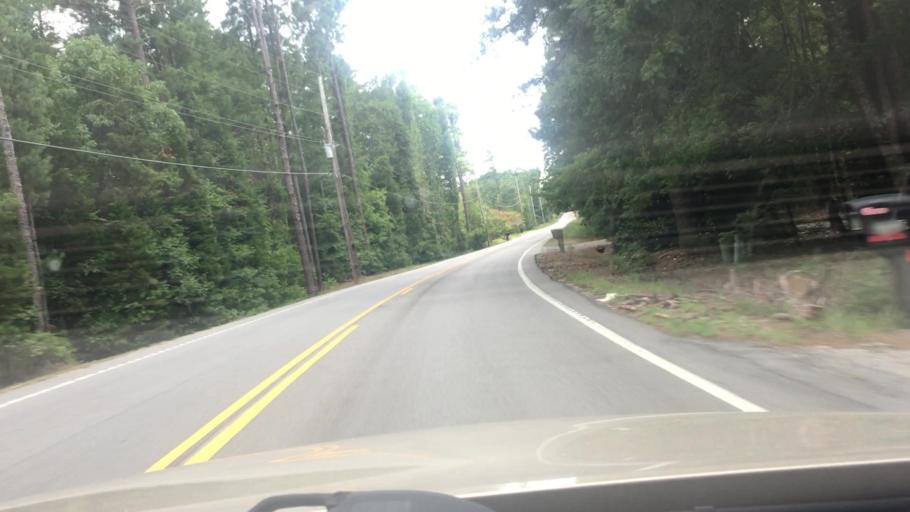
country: US
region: South Carolina
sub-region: Lexington County
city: Irmo
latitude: 34.1404
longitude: -81.1893
